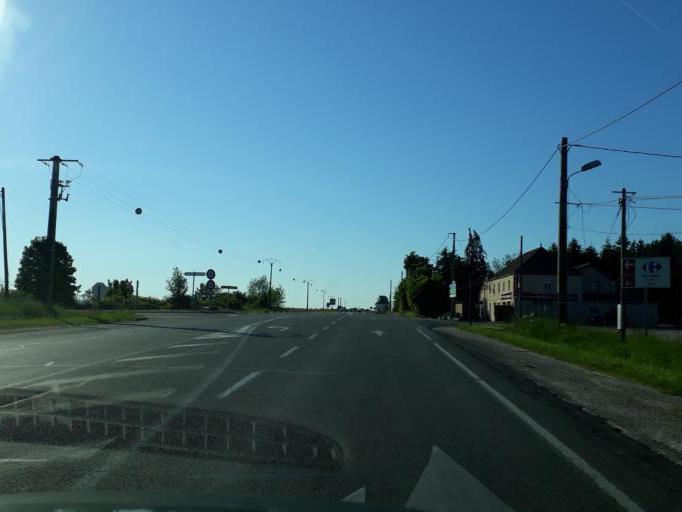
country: FR
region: Centre
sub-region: Departement du Loiret
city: Briare
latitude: 47.6077
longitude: 2.7771
